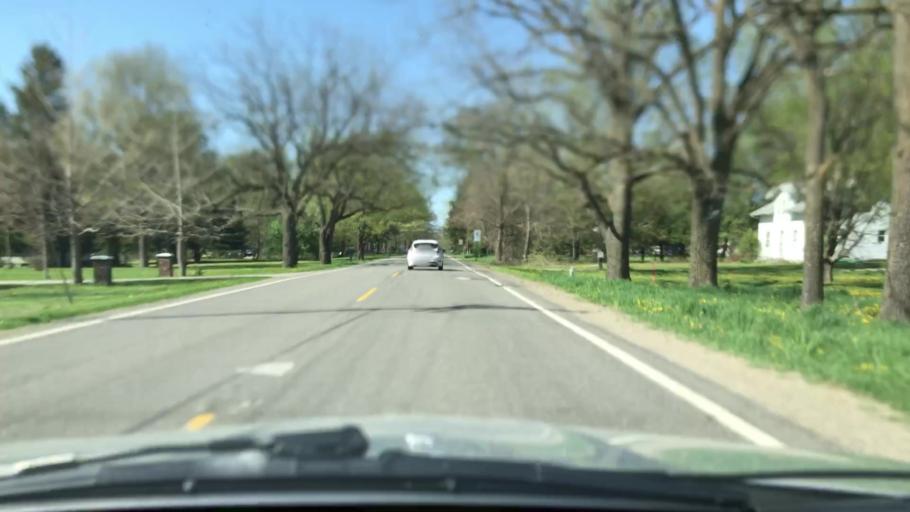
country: US
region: Indiana
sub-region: Saint Joseph County
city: Georgetown
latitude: 41.7606
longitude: -86.3038
